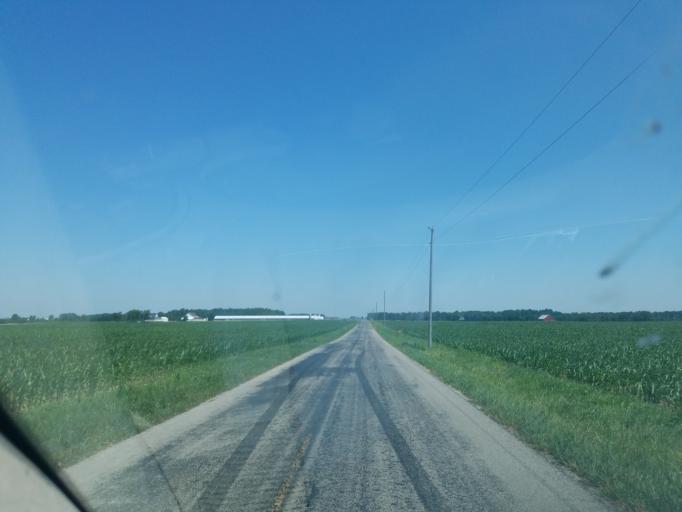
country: US
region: Ohio
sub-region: Mercer County
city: Saint Henry
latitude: 40.4608
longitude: -84.7080
